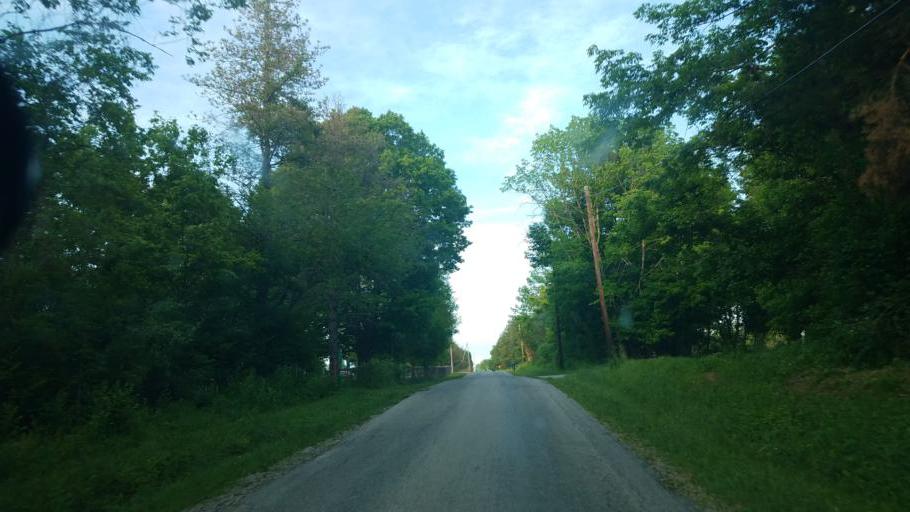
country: US
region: Ohio
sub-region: Highland County
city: Greenfield
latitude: 39.2780
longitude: -83.4120
